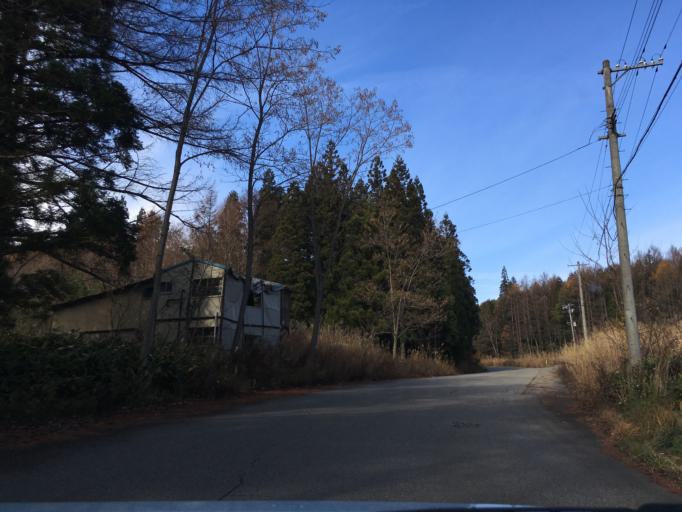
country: JP
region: Fukushima
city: Inawashiro
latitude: 37.4525
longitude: 140.0096
